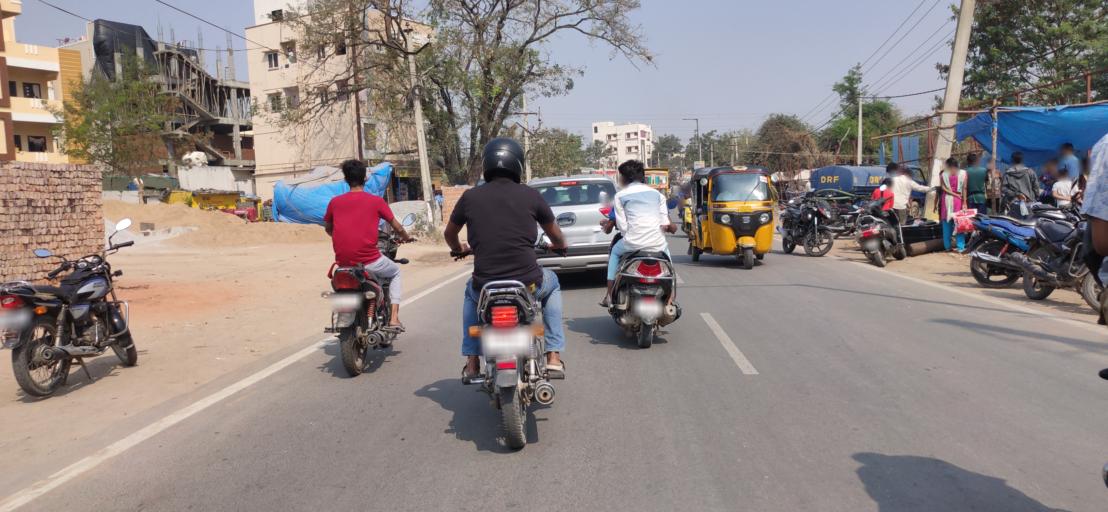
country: IN
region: Telangana
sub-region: Rangareddi
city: Kukatpalli
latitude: 17.5027
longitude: 78.4082
